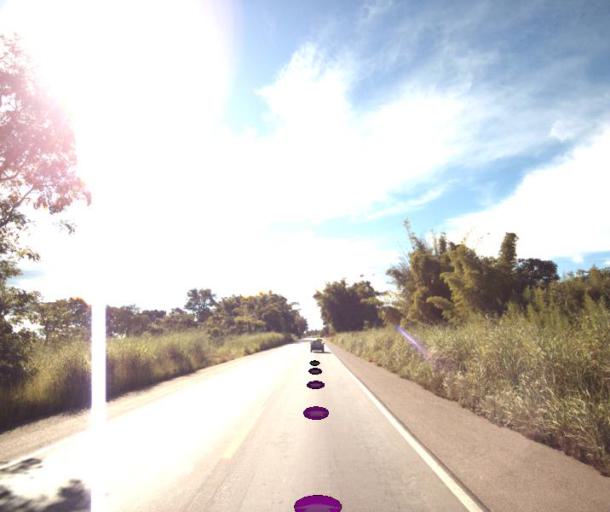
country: BR
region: Goias
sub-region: Uruana
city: Uruana
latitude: -15.5148
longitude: -49.4715
